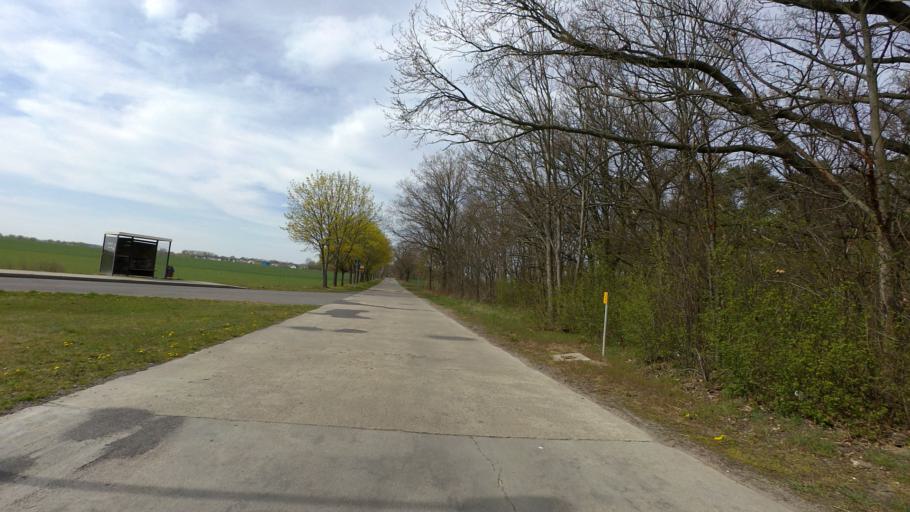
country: DE
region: Brandenburg
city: Schonefeld
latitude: 52.3371
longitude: 13.5365
